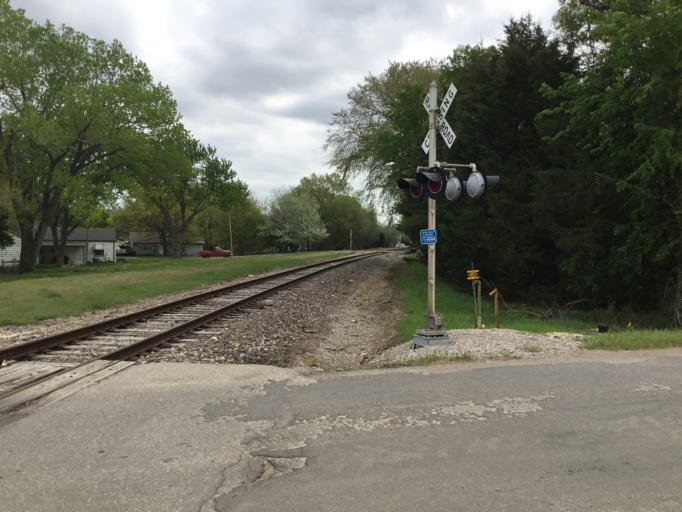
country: US
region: Kansas
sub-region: Butler County
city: El Dorado
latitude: 37.8264
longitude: -96.8591
